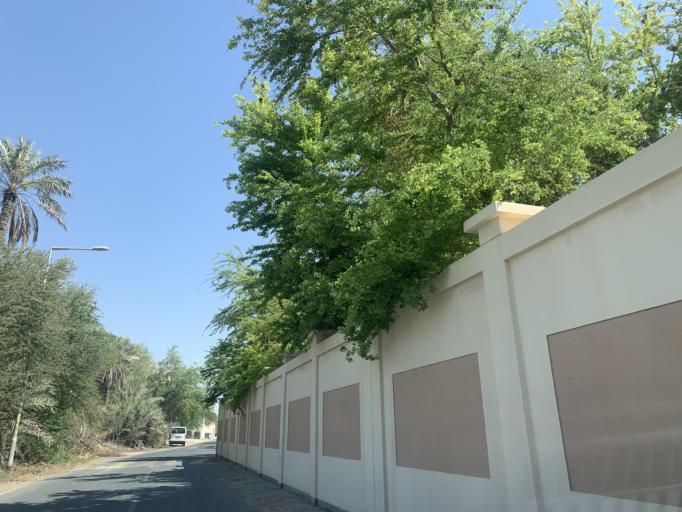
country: BH
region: Manama
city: Jidd Hafs
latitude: 26.2260
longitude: 50.4990
